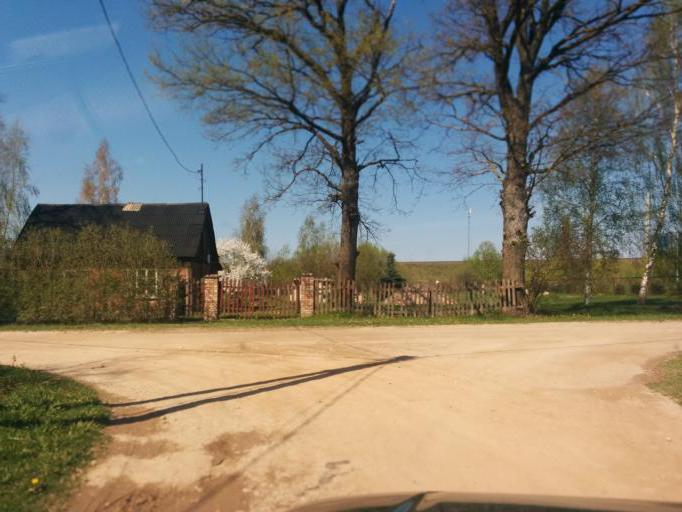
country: LV
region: Jelgava
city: Jelgava
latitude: 56.6305
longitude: 23.7092
